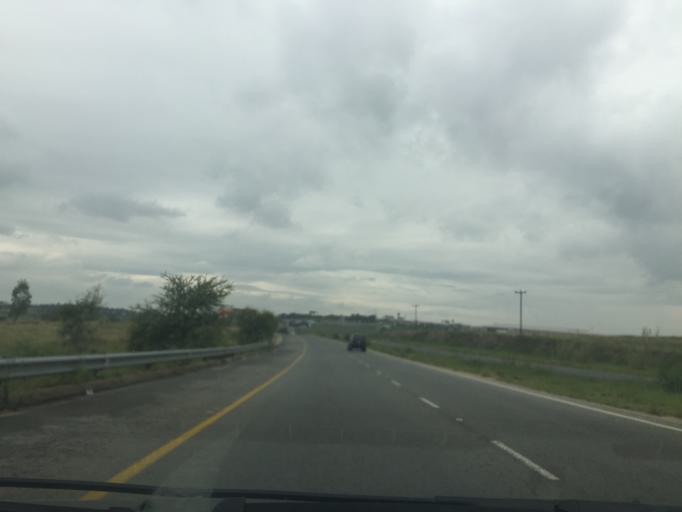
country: ZA
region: Gauteng
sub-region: City of Johannesburg Metropolitan Municipality
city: Diepsloot
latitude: -25.9410
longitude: 27.9124
